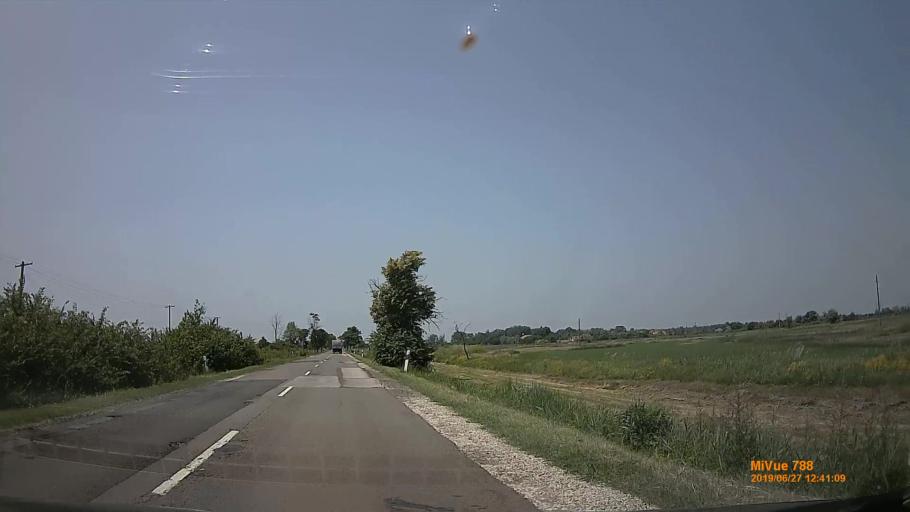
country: HU
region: Pest
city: Tortel
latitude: 47.1795
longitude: 19.9009
